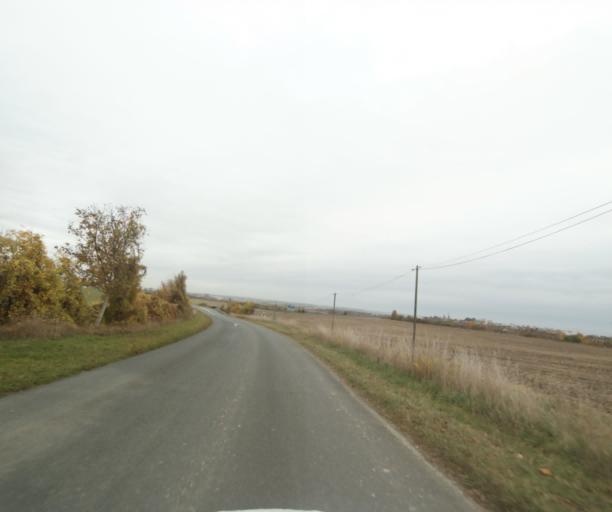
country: FR
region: Poitou-Charentes
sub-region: Departement de la Charente-Maritime
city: Chermignac
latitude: 45.7201
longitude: -0.6584
